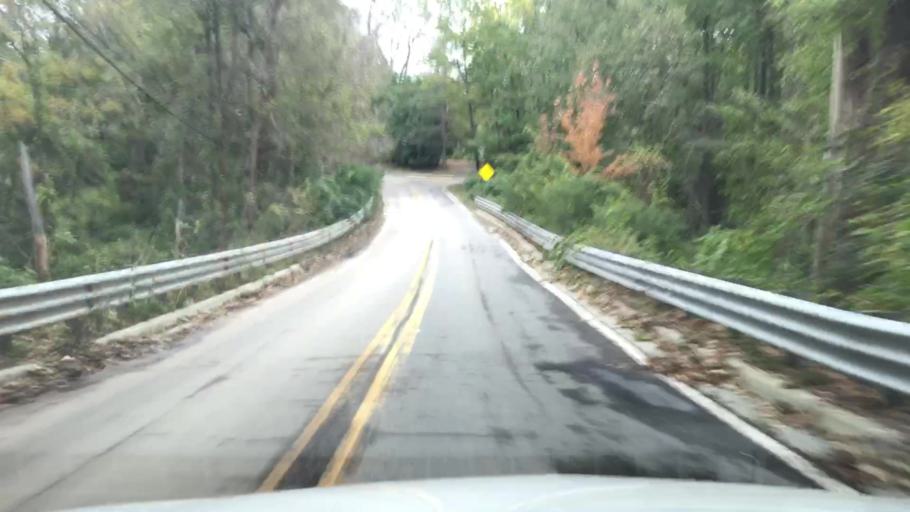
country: US
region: Michigan
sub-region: Oakland County
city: Rochester
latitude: 42.7434
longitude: -83.1213
